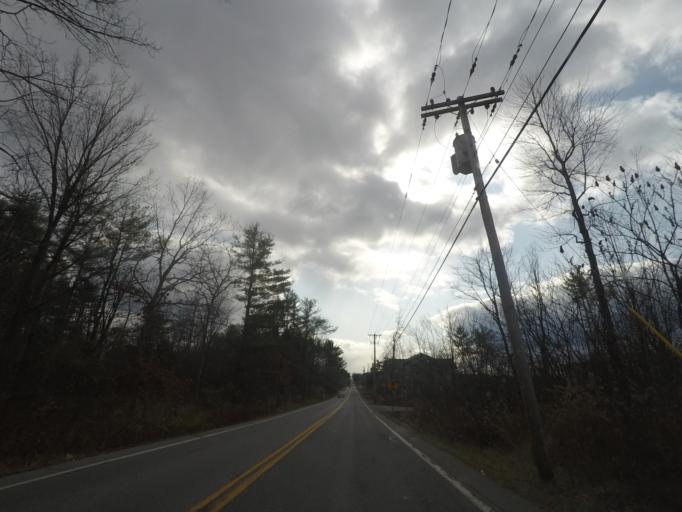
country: US
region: New York
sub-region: Saratoga County
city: Ballston Spa
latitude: 42.9744
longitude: -73.8314
